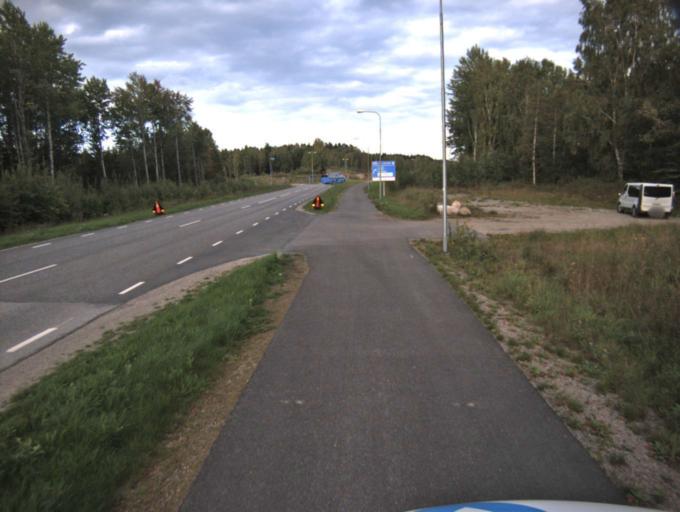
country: SE
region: Vaestra Goetaland
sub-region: Ulricehamns Kommun
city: Ulricehamn
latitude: 57.8058
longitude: 13.4511
